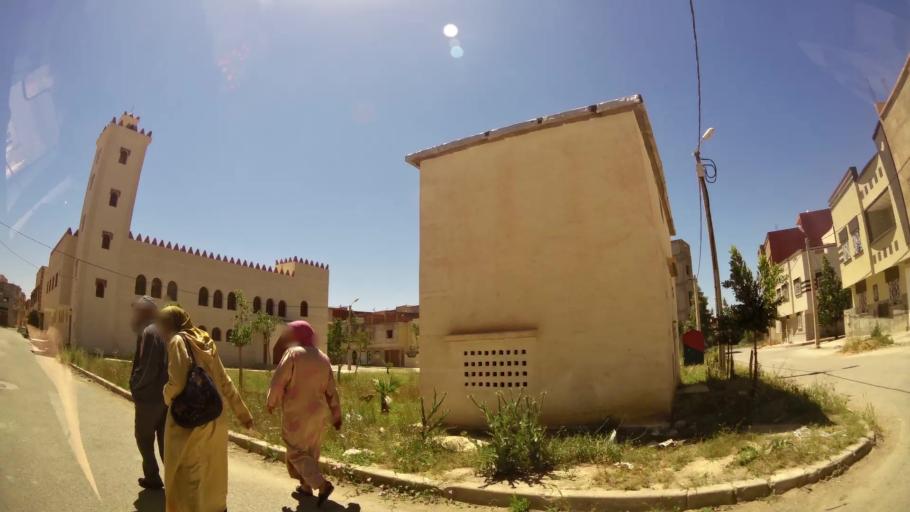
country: MA
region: Oriental
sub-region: Oujda-Angad
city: Oujda
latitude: 34.6815
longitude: -1.8641
